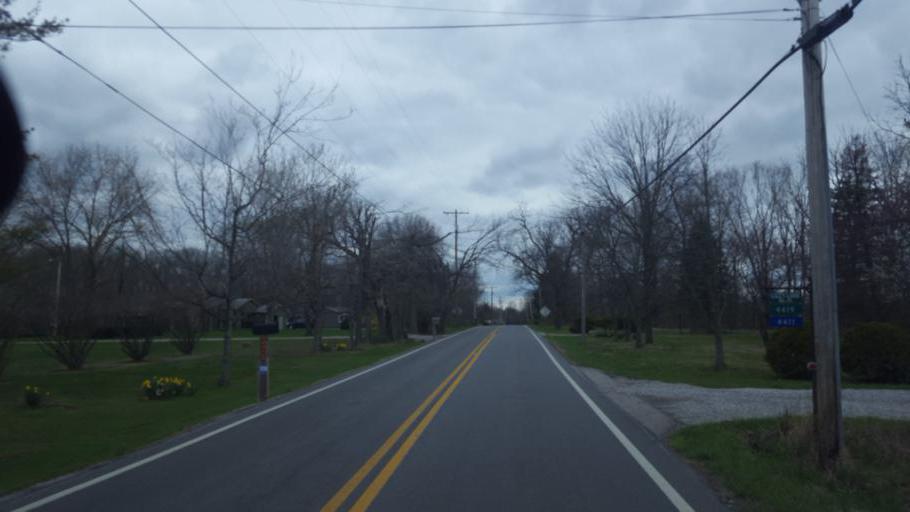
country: US
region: Ohio
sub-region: Delaware County
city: Sunbury
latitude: 40.1808
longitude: -82.8655
